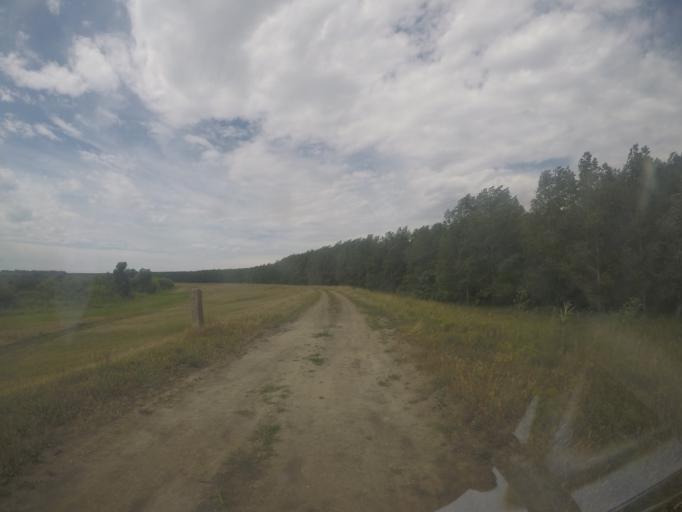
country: RS
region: Autonomna Pokrajina Vojvodina
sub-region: Juznobacki Okrug
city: Titel
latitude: 45.1738
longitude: 20.2855
